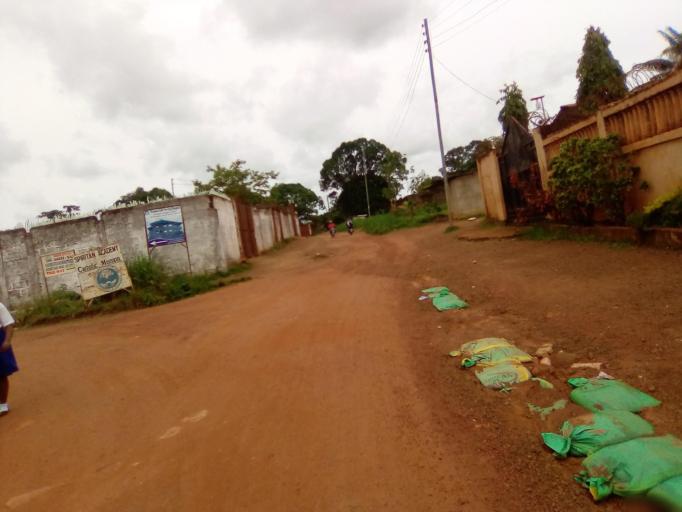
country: SL
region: Southern Province
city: Bo
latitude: 7.9468
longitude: -11.7190
